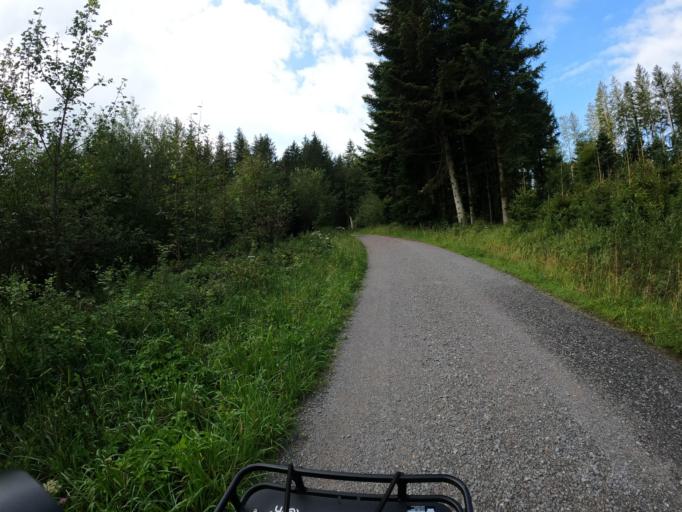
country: CH
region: Aargau
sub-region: Bezirk Muri
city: Buttwil
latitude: 47.2294
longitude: 8.3183
